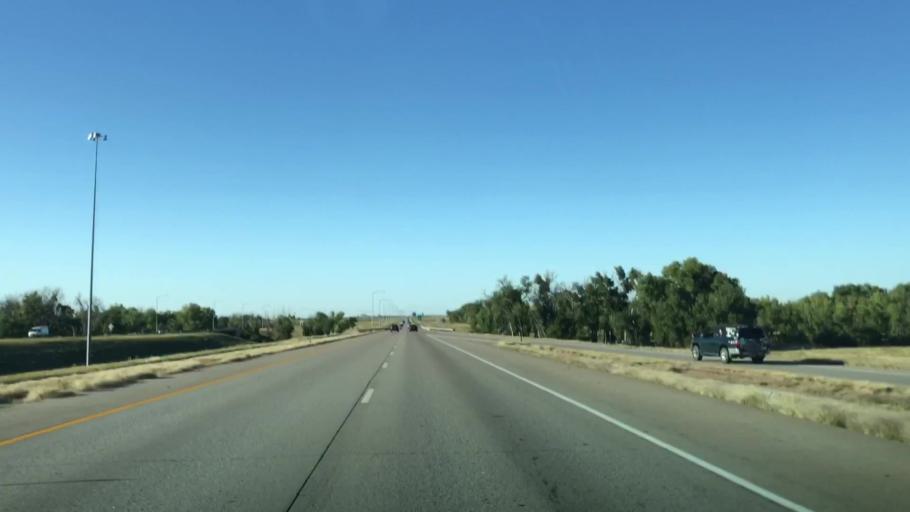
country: US
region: Colorado
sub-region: Adams County
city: Aurora
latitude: 39.8010
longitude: -104.7863
